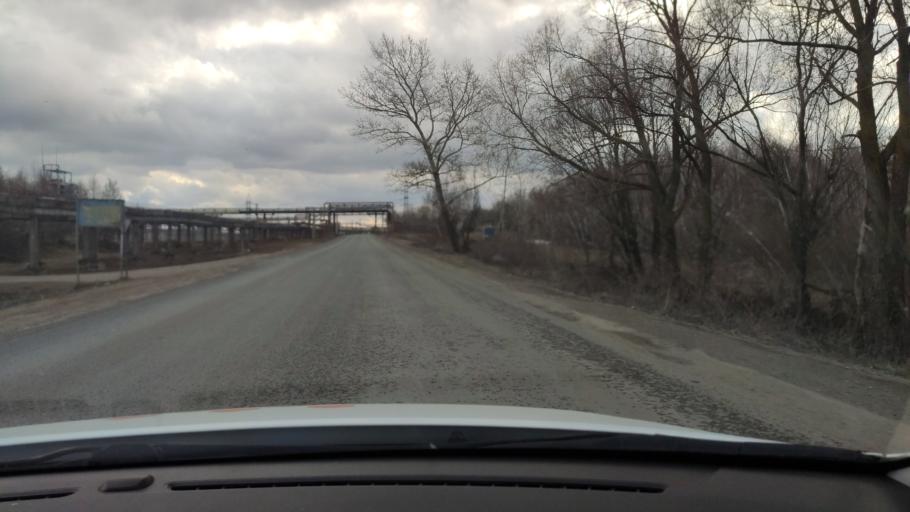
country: RU
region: Tatarstan
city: Staroye Arakchino
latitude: 55.8817
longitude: 48.9761
